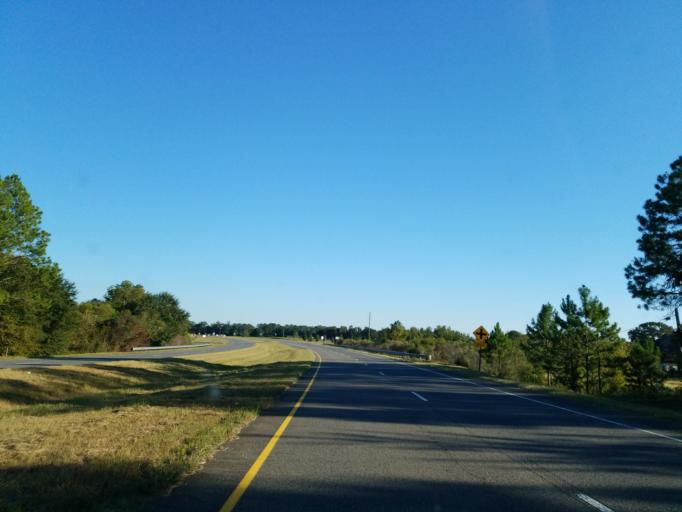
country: US
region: Georgia
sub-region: Lee County
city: Leesburg
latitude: 31.7260
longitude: -84.1816
